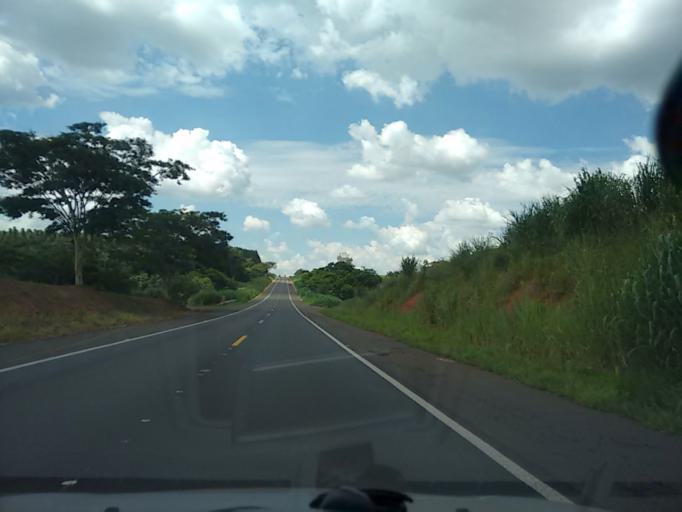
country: BR
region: Sao Paulo
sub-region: Osvaldo Cruz
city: Osvaldo Cruz
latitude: -21.8403
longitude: -50.8275
